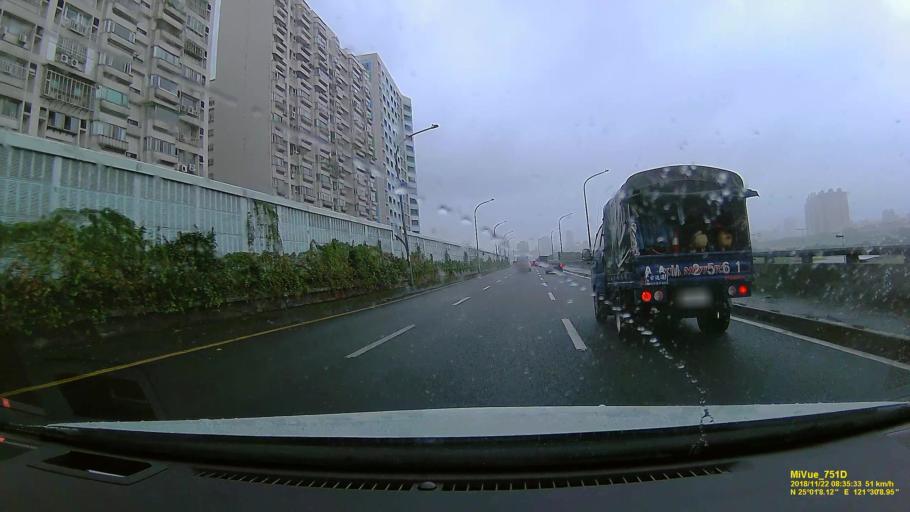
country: TW
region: Taipei
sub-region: Taipei
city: Banqiao
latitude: 25.0191
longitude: 121.5027
